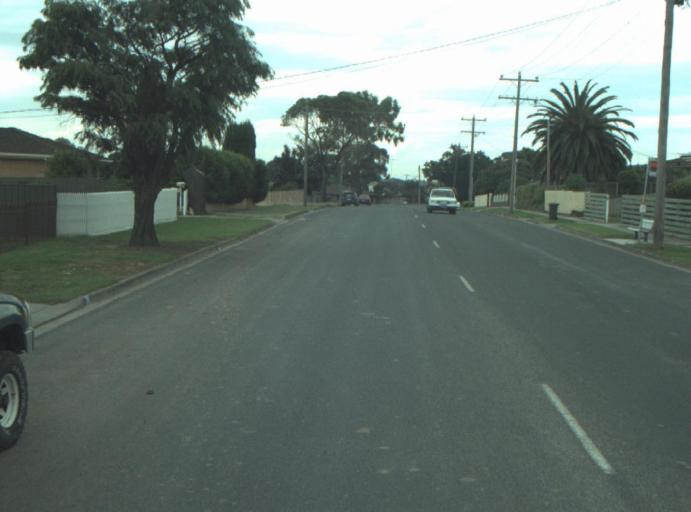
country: AU
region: Victoria
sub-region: Greater Geelong
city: Breakwater
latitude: -38.1788
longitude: 144.3678
